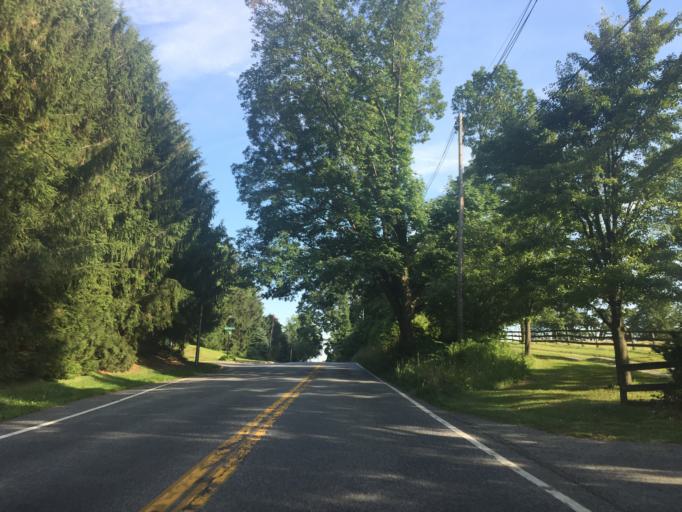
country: US
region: Maryland
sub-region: Harford County
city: Jarrettsville
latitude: 39.6107
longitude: -76.5154
